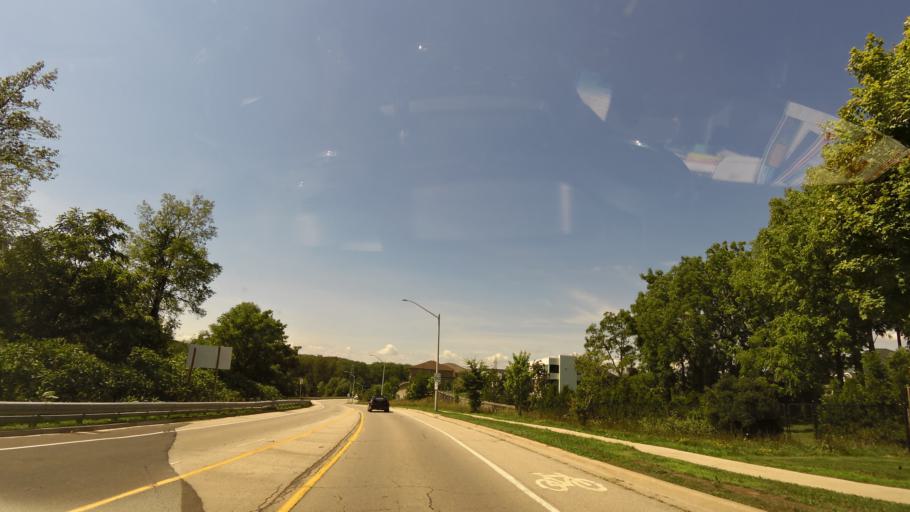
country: CA
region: Ontario
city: Ancaster
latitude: 43.2202
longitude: -79.9254
